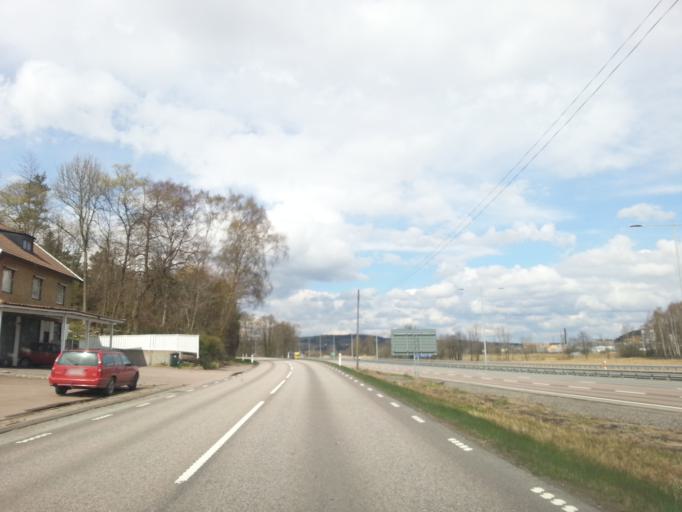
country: SE
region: Vaestra Goetaland
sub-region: Ale Kommun
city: Surte
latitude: 57.8421
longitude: 12.0050
